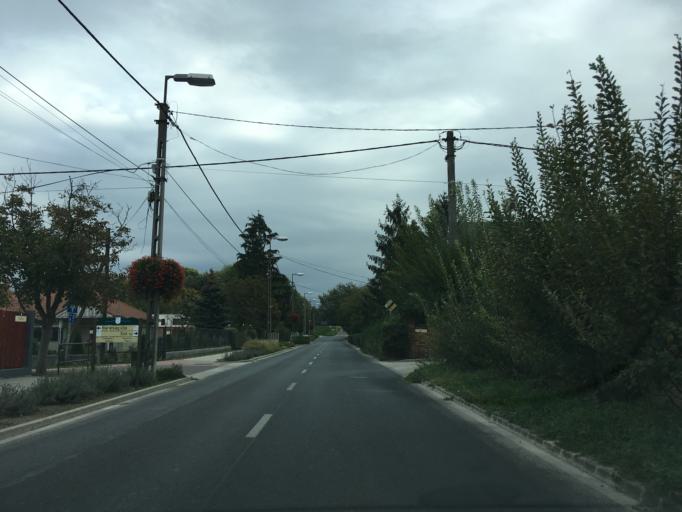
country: HU
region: Pest
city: Szazhalombatta
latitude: 47.3115
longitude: 18.9249
